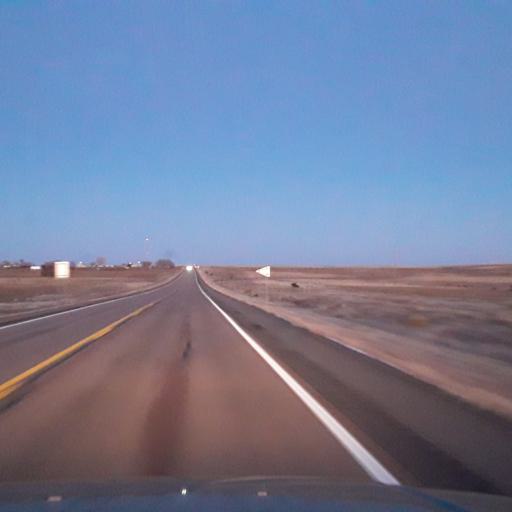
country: US
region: New Mexico
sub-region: Guadalupe County
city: Santa Rosa
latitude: 34.7760
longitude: -104.9534
